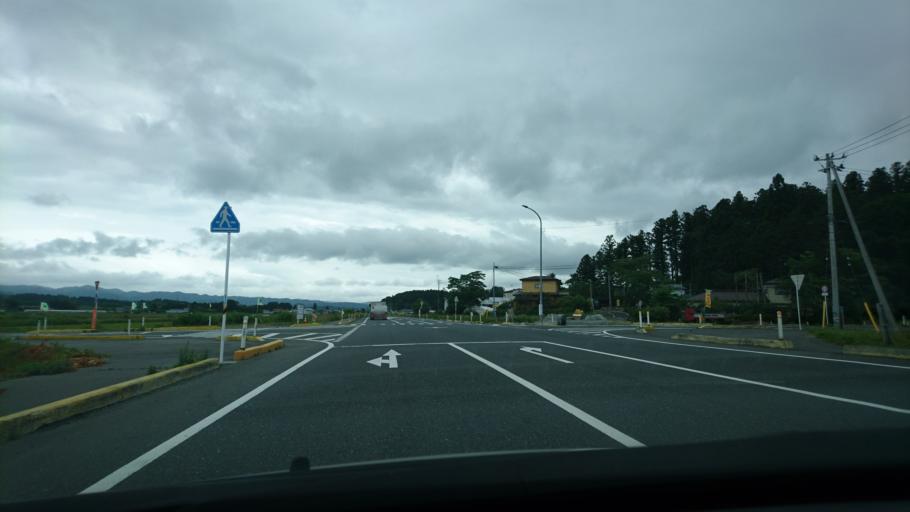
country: JP
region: Iwate
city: Ichinoseki
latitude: 38.7405
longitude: 141.2558
